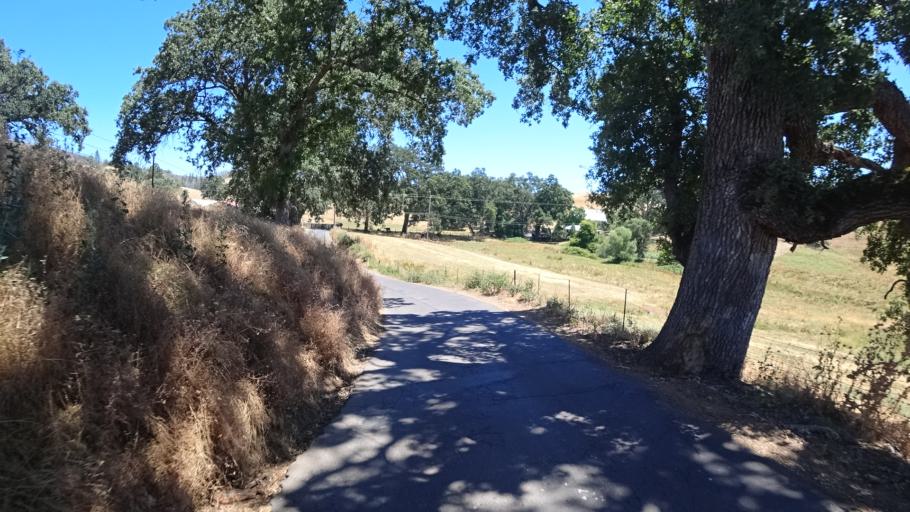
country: US
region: California
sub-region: Calaveras County
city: Mountain Ranch
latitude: 38.2364
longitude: -120.5579
